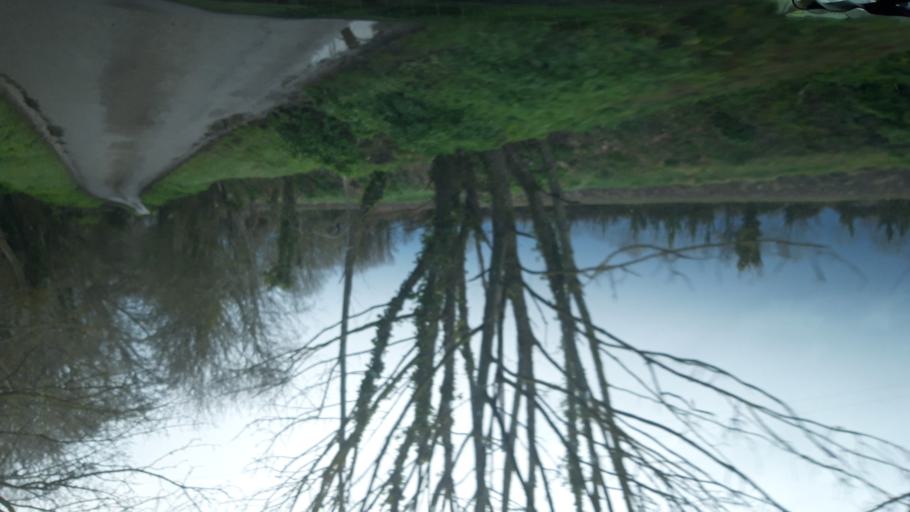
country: IE
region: Leinster
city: Donabate
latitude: 53.4744
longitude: -6.1688
